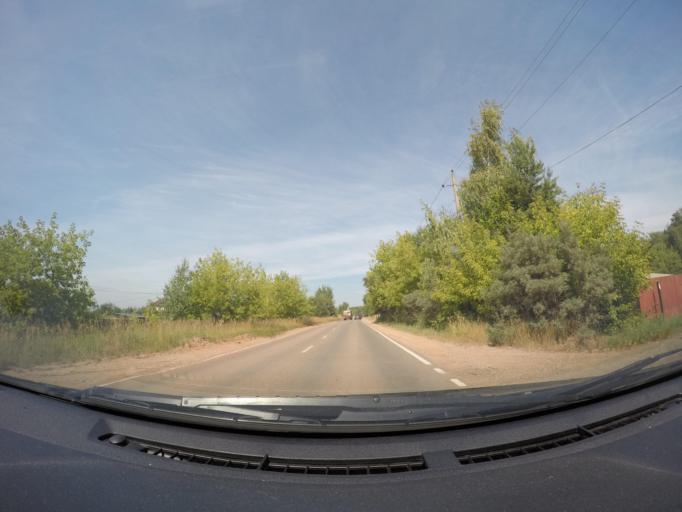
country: RU
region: Moskovskaya
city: Rechitsy
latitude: 55.6219
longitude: 38.4380
